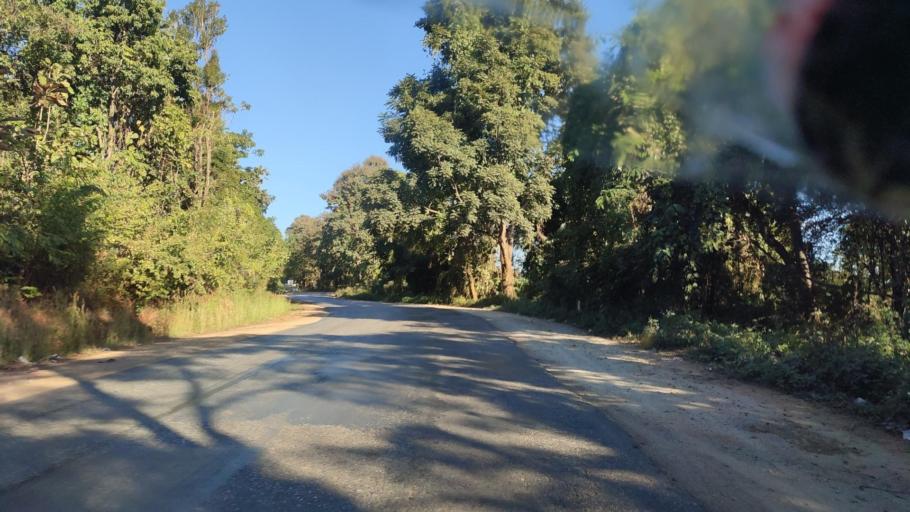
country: MM
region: Mandalay
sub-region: Pyin Oo Lwin District
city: Pyin Oo Lwin
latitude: 22.3539
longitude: 96.8426
